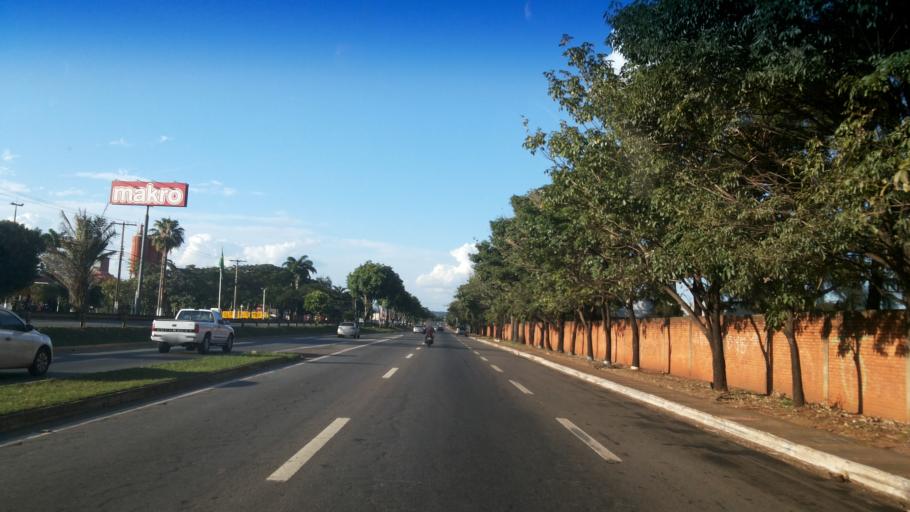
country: BR
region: Goias
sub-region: Goiania
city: Goiania
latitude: -16.6476
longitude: -49.3105
